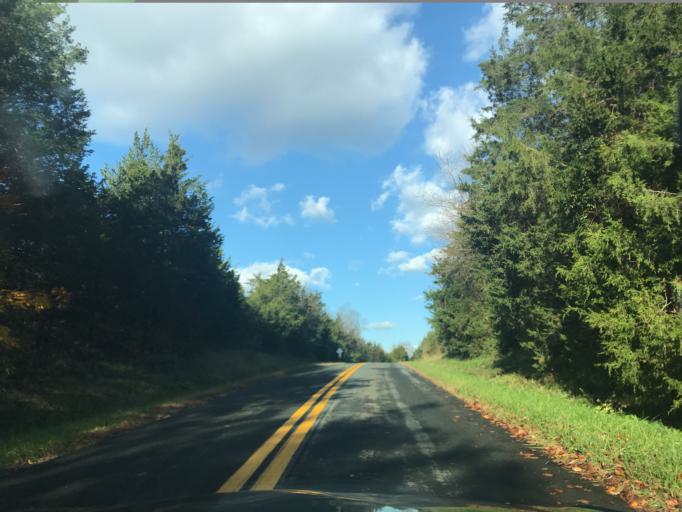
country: US
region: Maryland
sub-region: Carroll County
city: New Windsor
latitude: 39.6208
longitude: -77.0928
